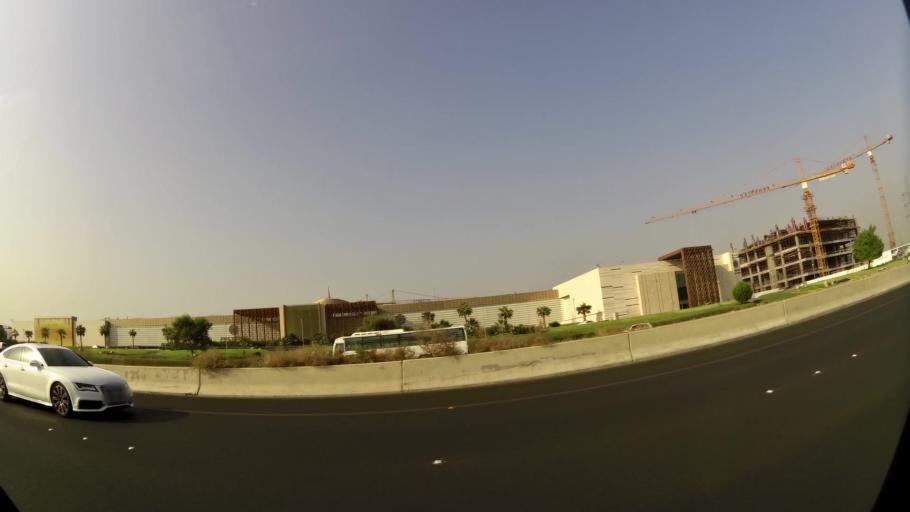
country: KW
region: Al Asimah
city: Ar Rabiyah
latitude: 29.3012
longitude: 47.9406
